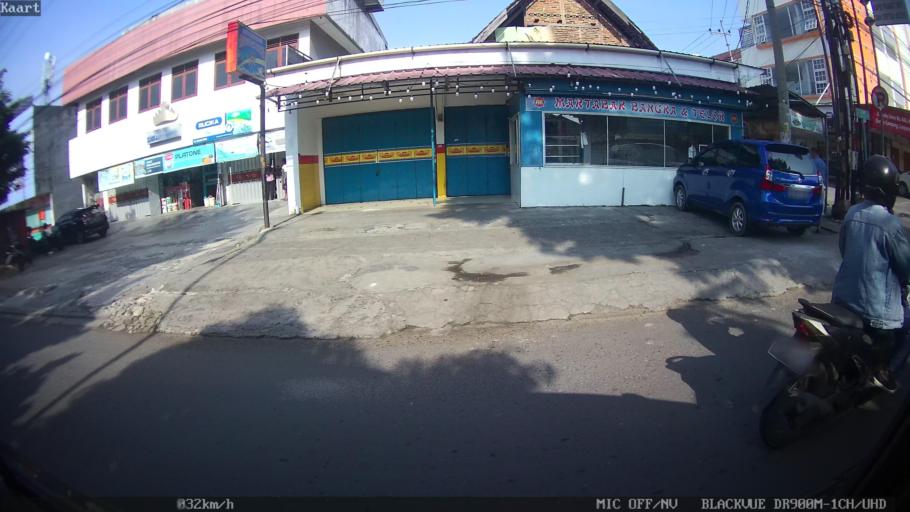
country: ID
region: Lampung
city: Kedaton
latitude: -5.3935
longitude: 105.2615
